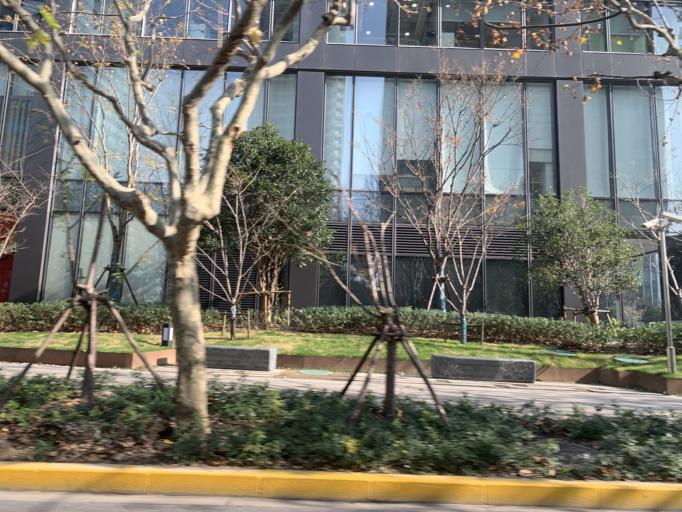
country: CN
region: Shanghai Shi
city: Hongkou
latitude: 31.2358
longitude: 121.4976
